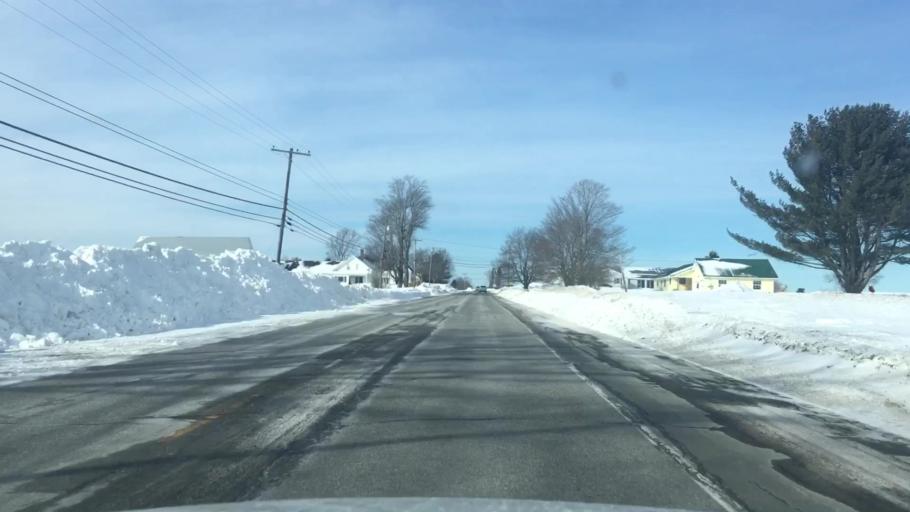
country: US
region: Maine
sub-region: Penobscot County
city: Charleston
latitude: 45.0241
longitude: -69.0298
